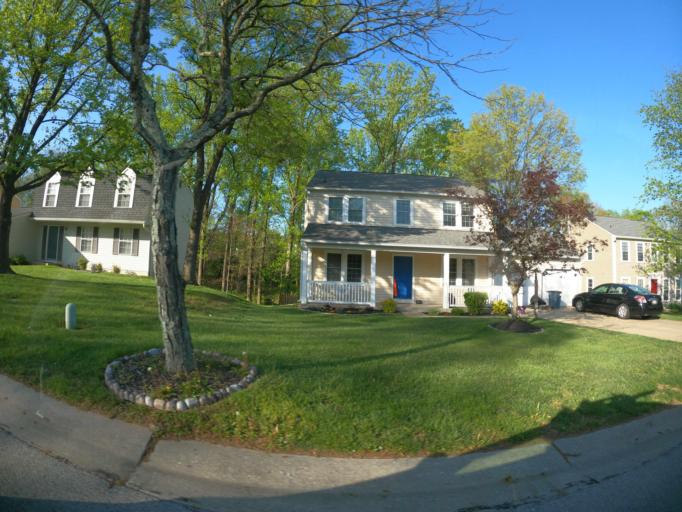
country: US
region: Maryland
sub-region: Howard County
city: Columbia
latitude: 39.2122
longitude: -76.8099
